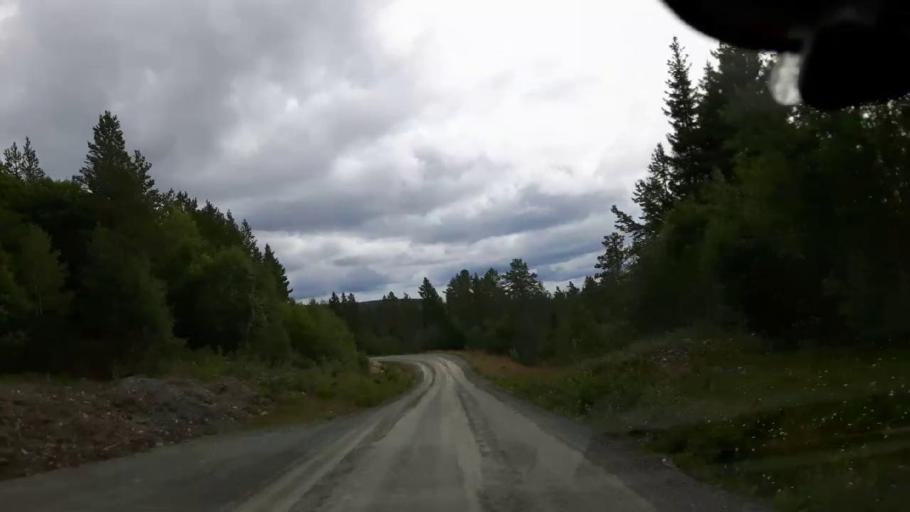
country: SE
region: Jaemtland
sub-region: Krokoms Kommun
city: Valla
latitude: 63.6109
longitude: 14.1070
